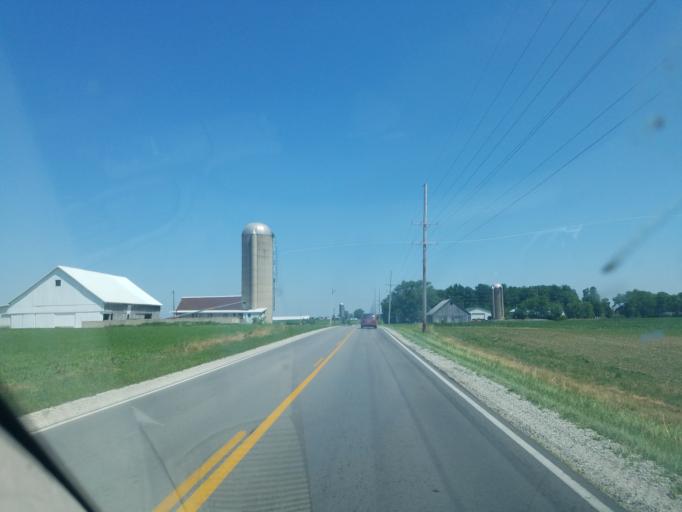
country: US
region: Ohio
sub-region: Mercer County
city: Saint Henry
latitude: 40.4331
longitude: -84.6483
